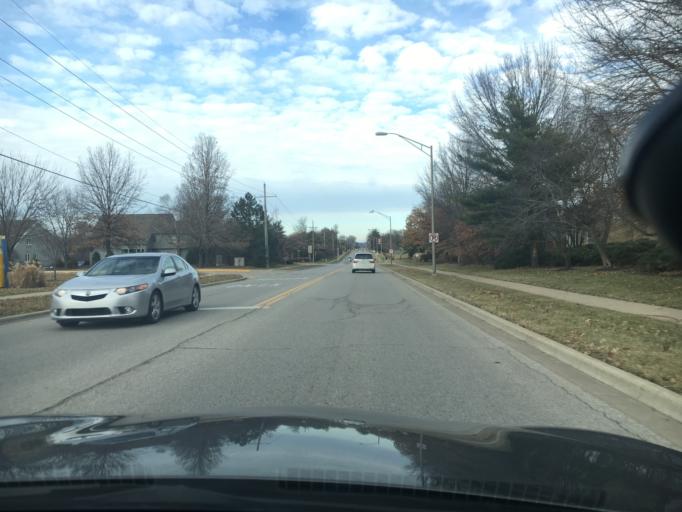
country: US
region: Kansas
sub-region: Johnson County
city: Leawood
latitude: 38.8874
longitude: -94.6305
